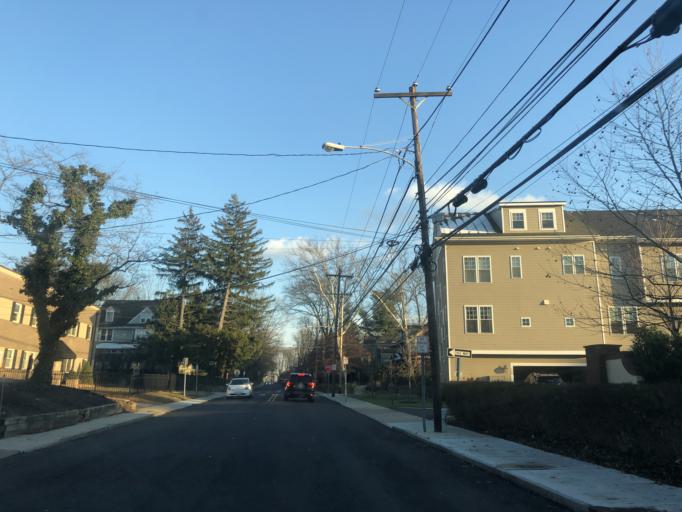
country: US
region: Pennsylvania
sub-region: Montgomery County
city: Bryn Mawr
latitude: 40.0192
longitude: -75.3185
